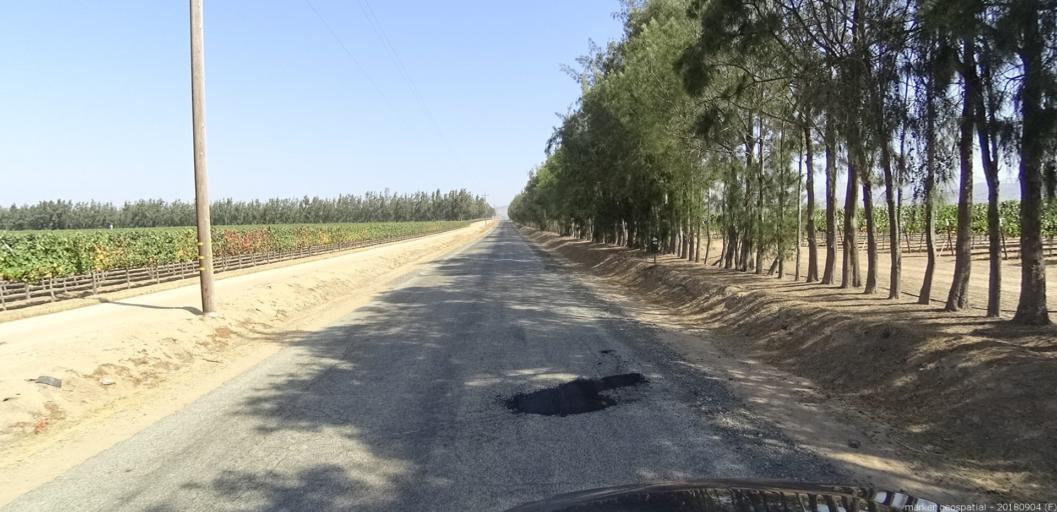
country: US
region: California
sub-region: Monterey County
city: Soledad
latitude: 36.4919
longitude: -121.3648
